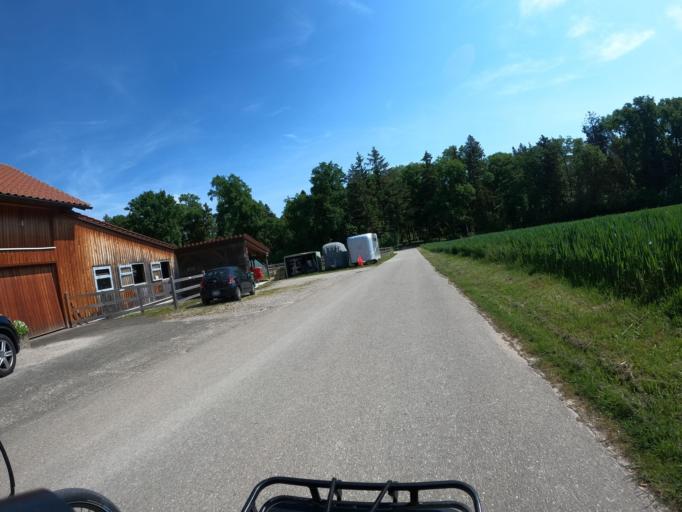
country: CH
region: Zurich
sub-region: Bezirk Dielsdorf
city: Niederhasli
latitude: 47.4859
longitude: 8.4888
